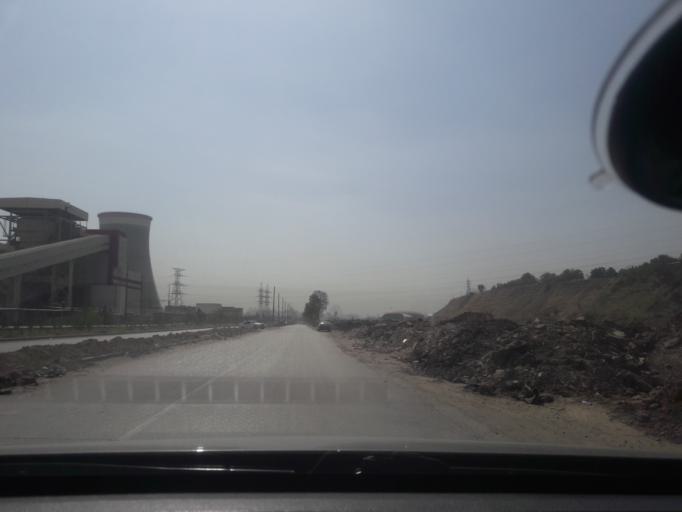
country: TJ
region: Dushanbe
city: Dushanbe
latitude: 38.6119
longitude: 68.7700
